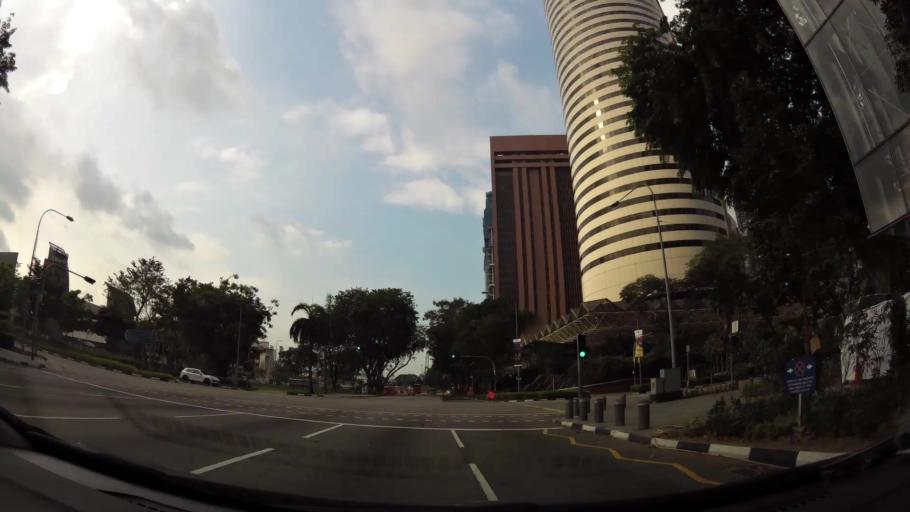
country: SG
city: Singapore
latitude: 1.2762
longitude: 103.8483
